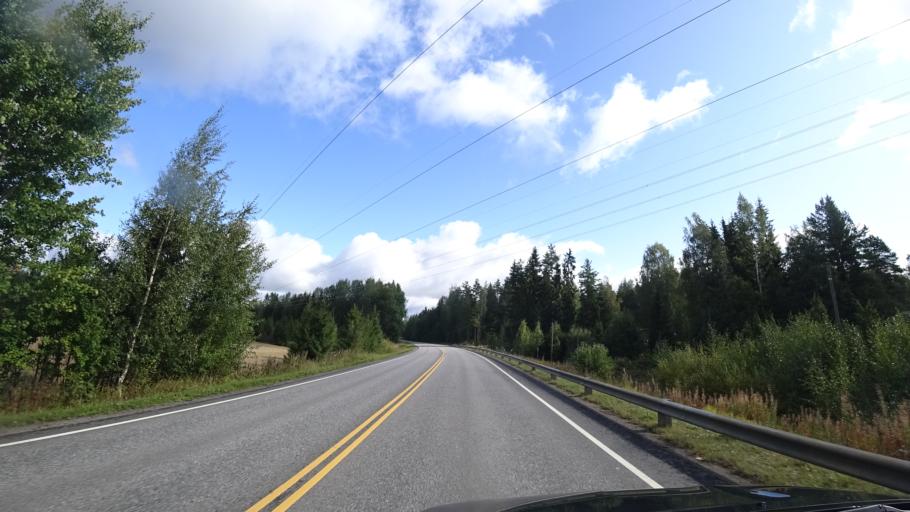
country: FI
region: Uusimaa
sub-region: Helsinki
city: Hyvinge
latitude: 60.5351
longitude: 24.9216
